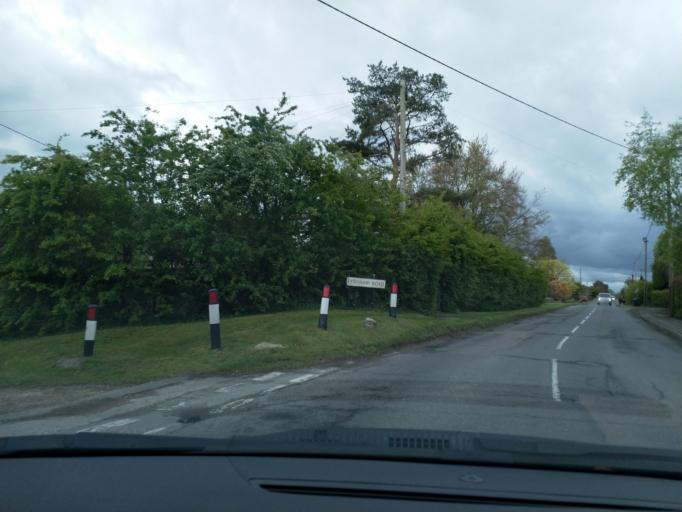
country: GB
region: England
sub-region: Oxfordshire
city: Eynsham
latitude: 51.7925
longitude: -1.3436
